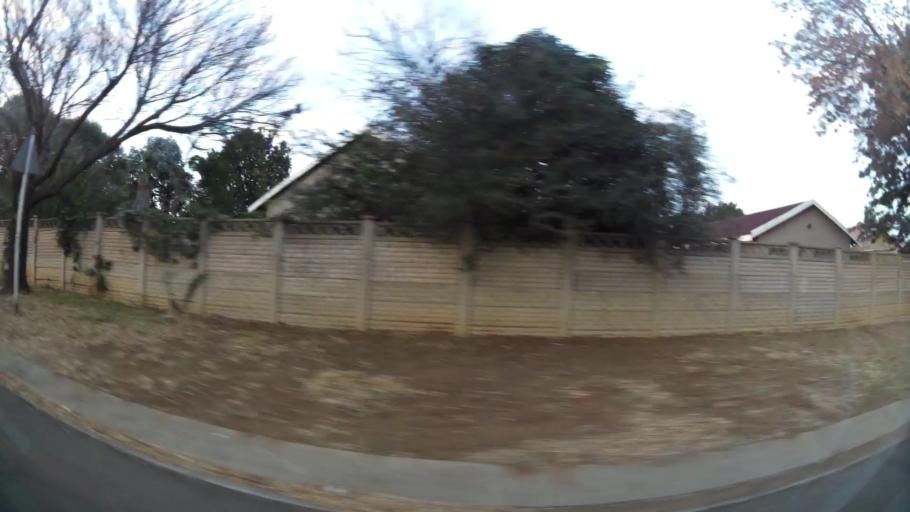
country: ZA
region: Orange Free State
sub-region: Mangaung Metropolitan Municipality
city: Bloemfontein
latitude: -29.1738
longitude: 26.1883
